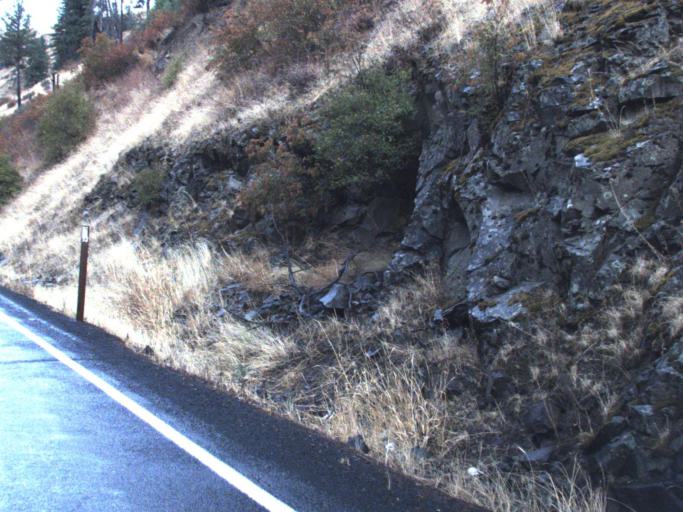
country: US
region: Washington
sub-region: Spokane County
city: Medical Lake
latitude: 47.7479
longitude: -117.8869
